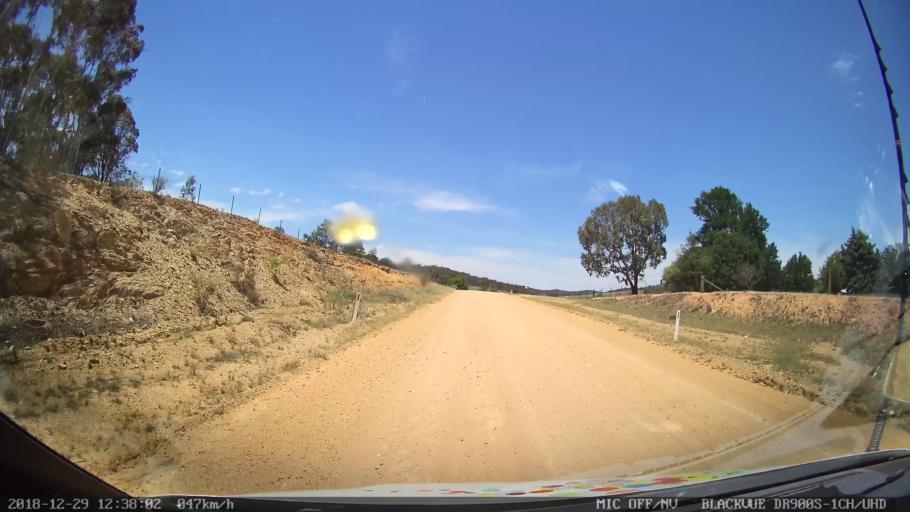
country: AU
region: Australian Capital Territory
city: Macarthur
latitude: -35.5855
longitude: 149.2291
